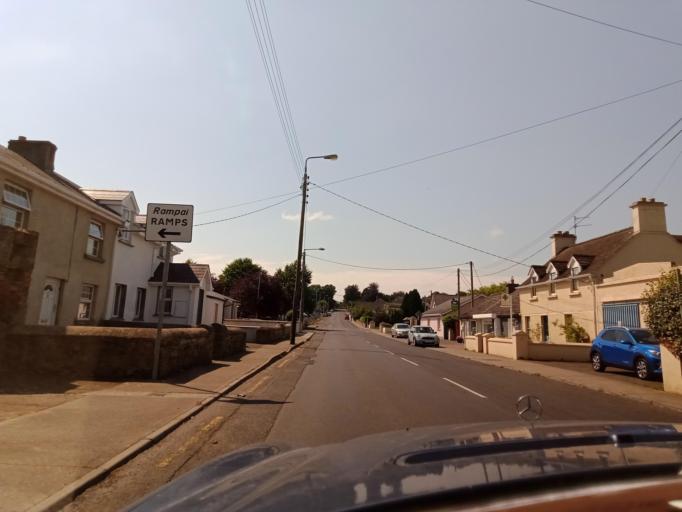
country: IE
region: Leinster
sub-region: Kilkenny
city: Piltown
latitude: 52.3513
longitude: -7.3322
